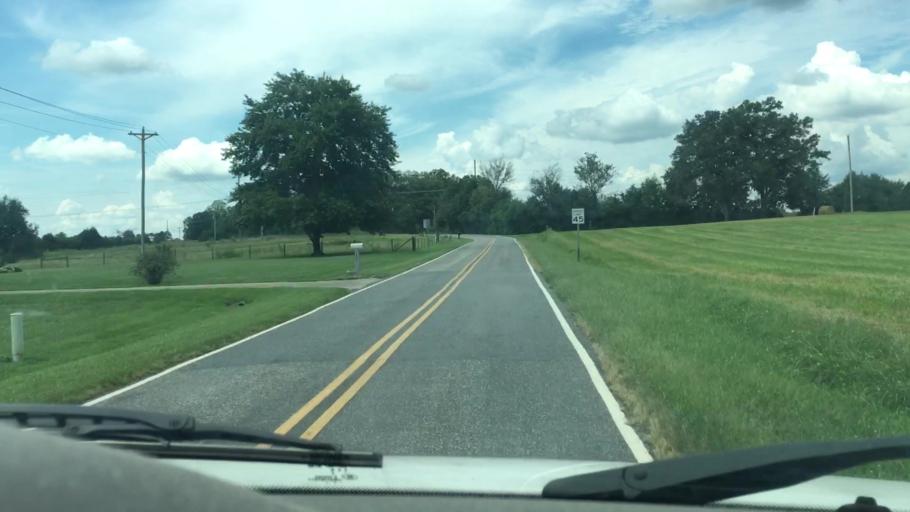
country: US
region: North Carolina
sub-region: Iredell County
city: Mooresville
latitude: 35.6635
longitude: -80.8174
